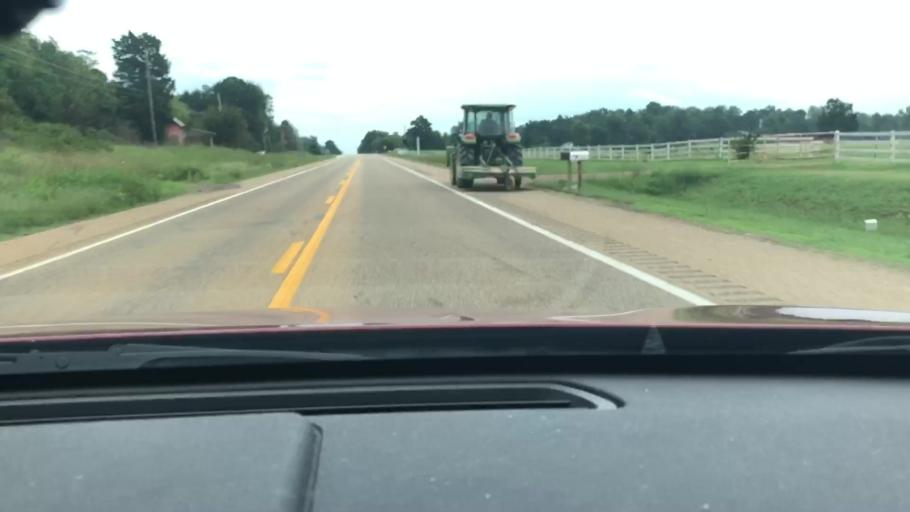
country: US
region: Arkansas
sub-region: Miller County
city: Texarkana
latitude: 33.4292
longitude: -93.9319
